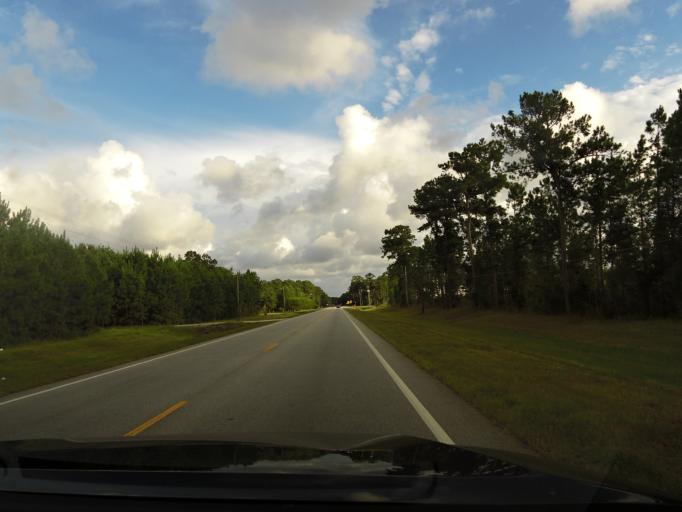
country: US
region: Georgia
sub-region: Liberty County
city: Midway
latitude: 31.7301
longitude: -81.4274
